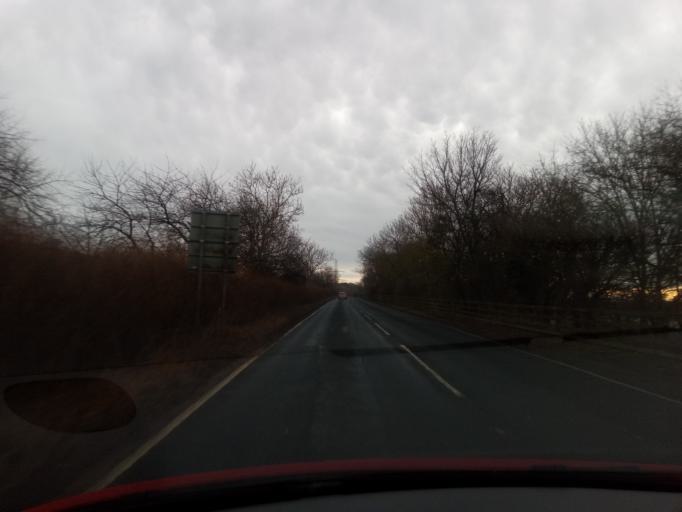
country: GB
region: England
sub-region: Northumberland
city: Wooler
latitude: 55.5418
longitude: -2.0073
